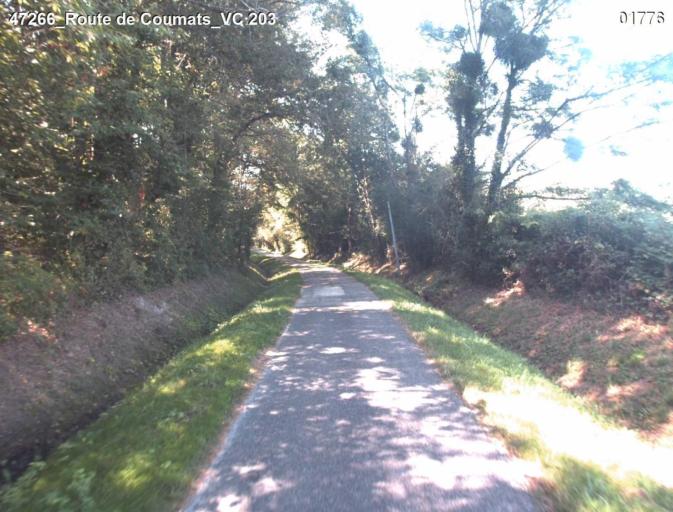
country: FR
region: Aquitaine
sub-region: Departement des Landes
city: Gabarret
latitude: 44.0041
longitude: 0.0972
